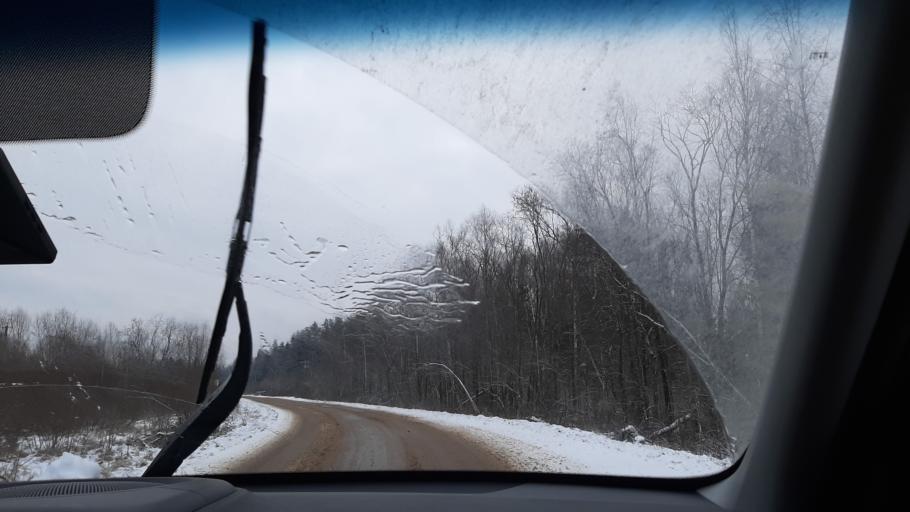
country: RU
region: Ivanovo
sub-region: Gorod Ivanovo
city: Ivanovo
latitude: 56.9227
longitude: 40.9835
